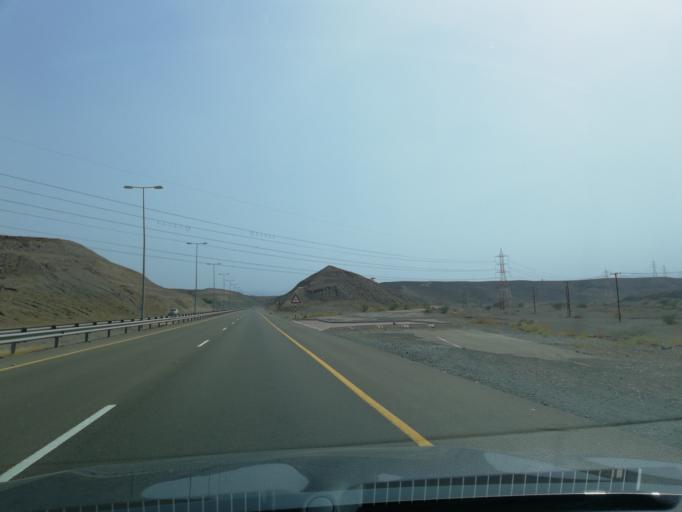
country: OM
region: Al Batinah
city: Al Liwa'
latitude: 24.3130
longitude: 56.4499
